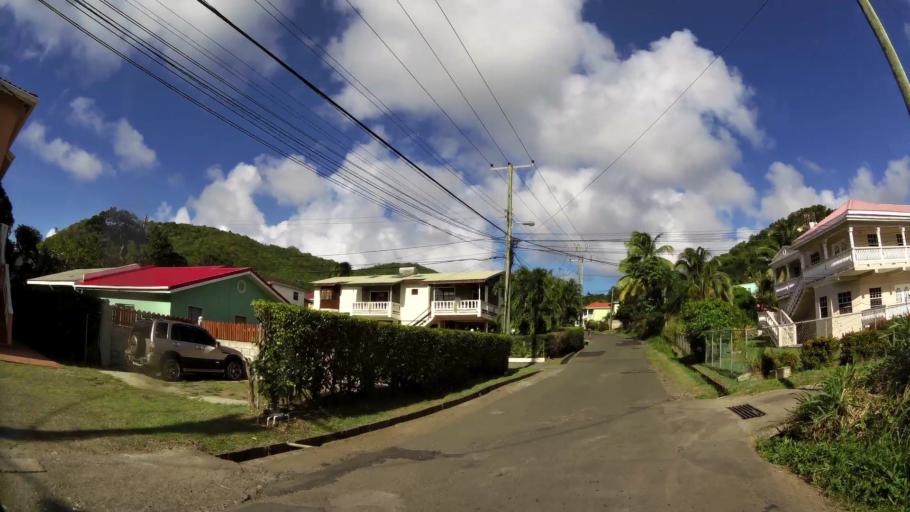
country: LC
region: Gros-Islet
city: Gros Islet
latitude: 14.0430
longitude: -60.9576
